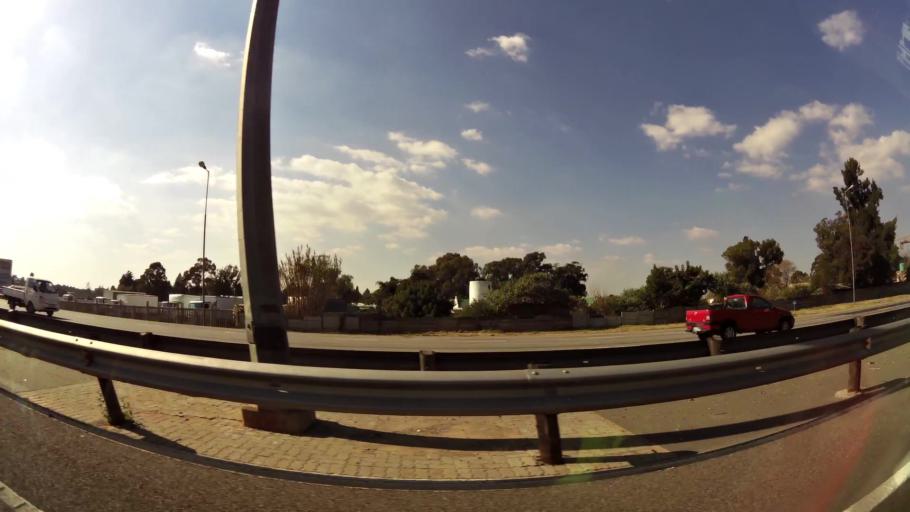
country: ZA
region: Gauteng
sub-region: Ekurhuleni Metropolitan Municipality
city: Tembisa
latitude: -26.0869
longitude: 28.2699
